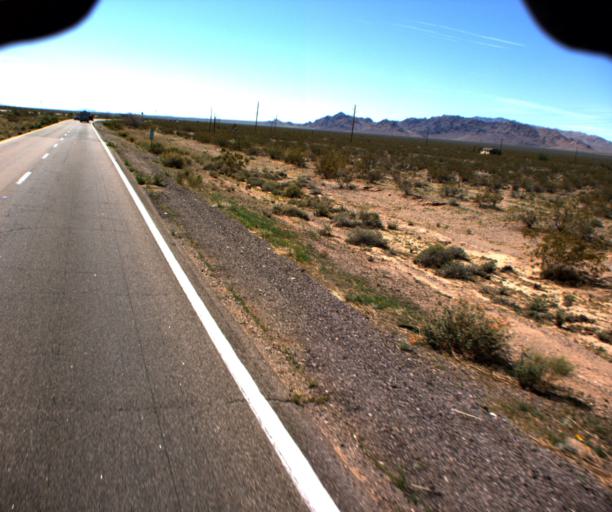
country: US
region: Arizona
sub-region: Mohave County
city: Dolan Springs
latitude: 35.6946
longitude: -114.4720
